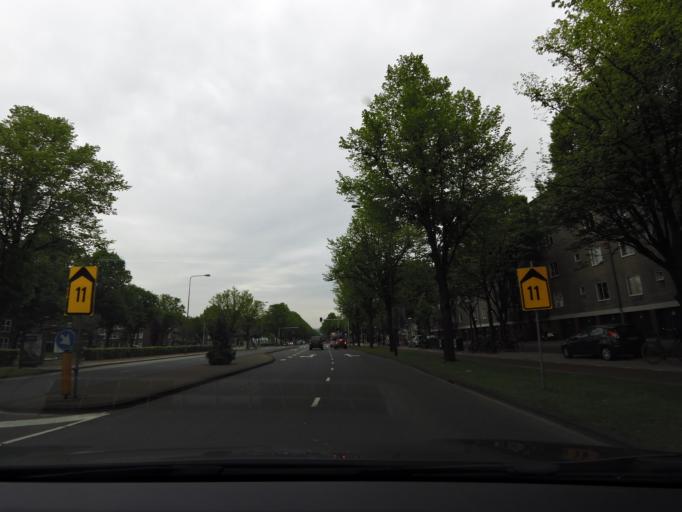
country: NL
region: North Holland
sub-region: Gemeente Amsterdam
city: Amsterdam
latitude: 52.3406
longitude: 4.8958
